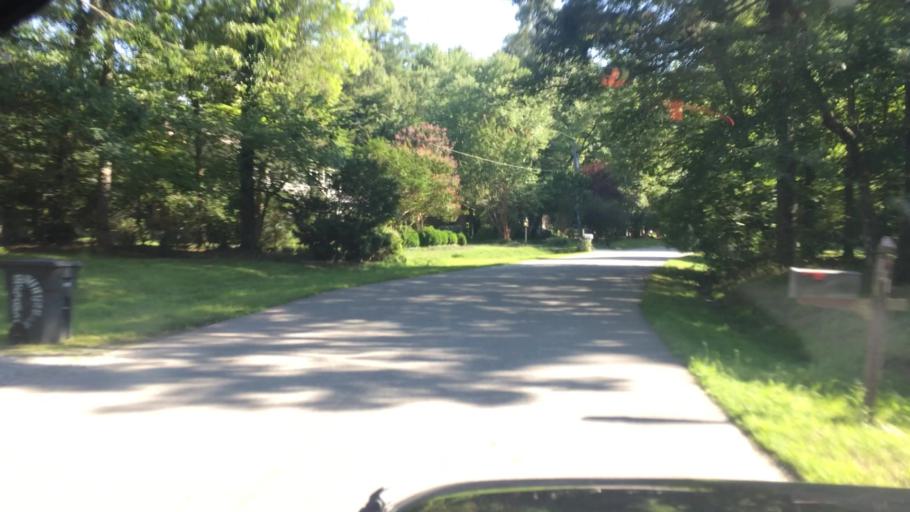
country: US
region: Virginia
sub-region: James City County
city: Williamsburg
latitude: 37.2389
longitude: -76.7969
